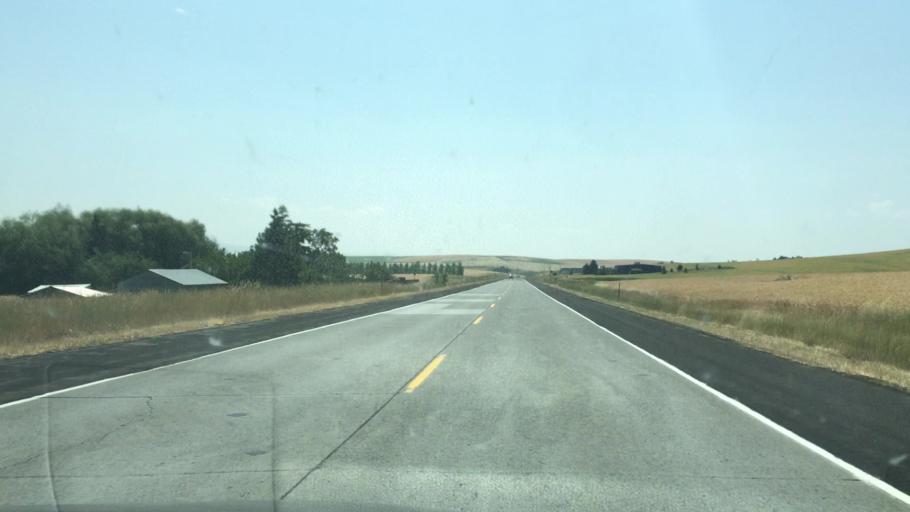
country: US
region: Idaho
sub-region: Lewis County
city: Nezperce
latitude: 46.0834
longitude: -116.3452
